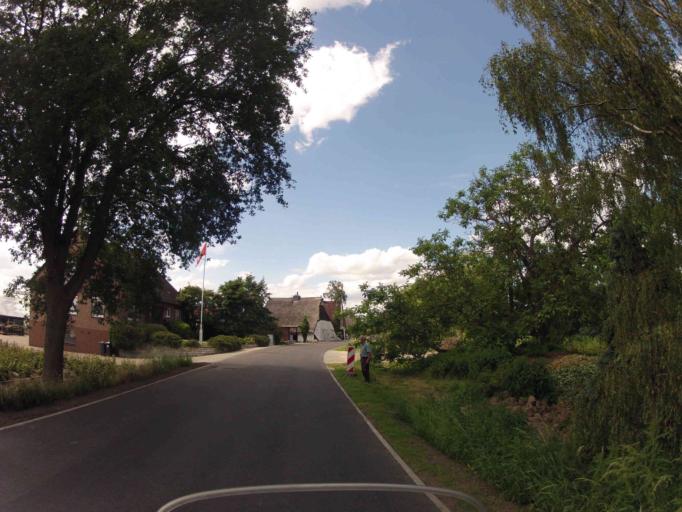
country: DE
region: Hamburg
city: Bergedorf
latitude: 53.4451
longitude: 10.1616
